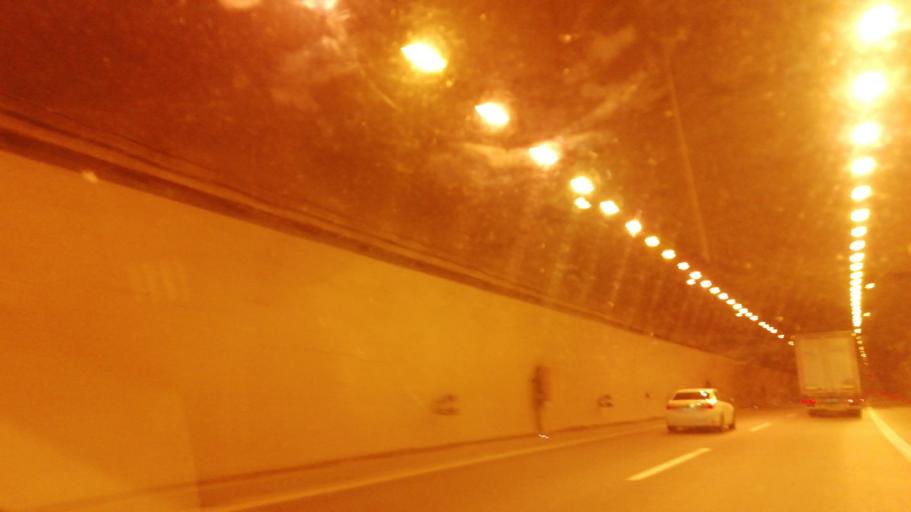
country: TR
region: Kocaeli
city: Izmit
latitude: 40.7784
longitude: 29.8887
